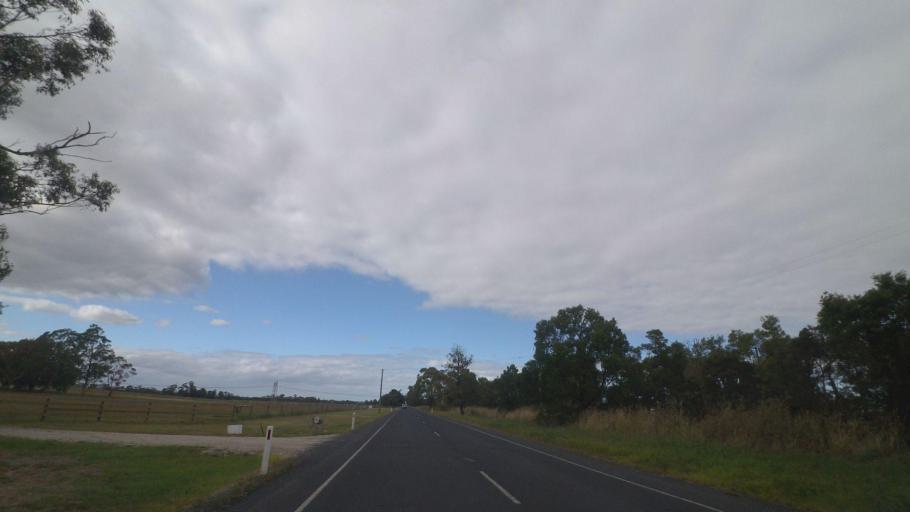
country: AU
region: Victoria
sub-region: Cardinia
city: Pakenham South
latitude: -38.1056
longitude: 145.5650
